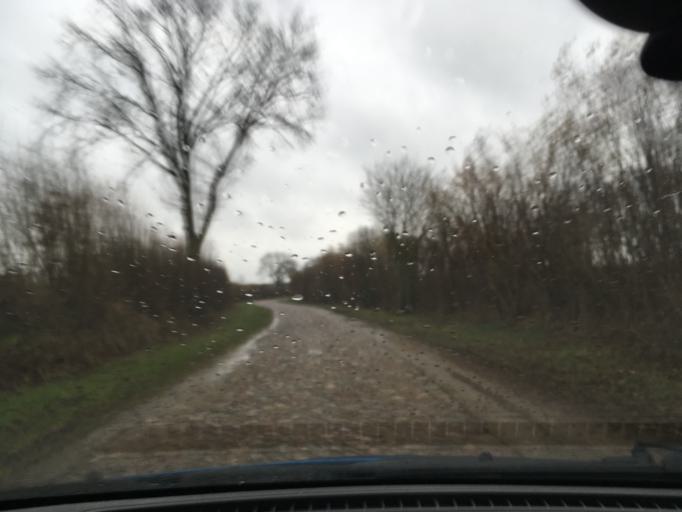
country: DE
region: Schleswig-Holstein
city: Schnakenbek
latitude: 53.3959
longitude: 10.5089
